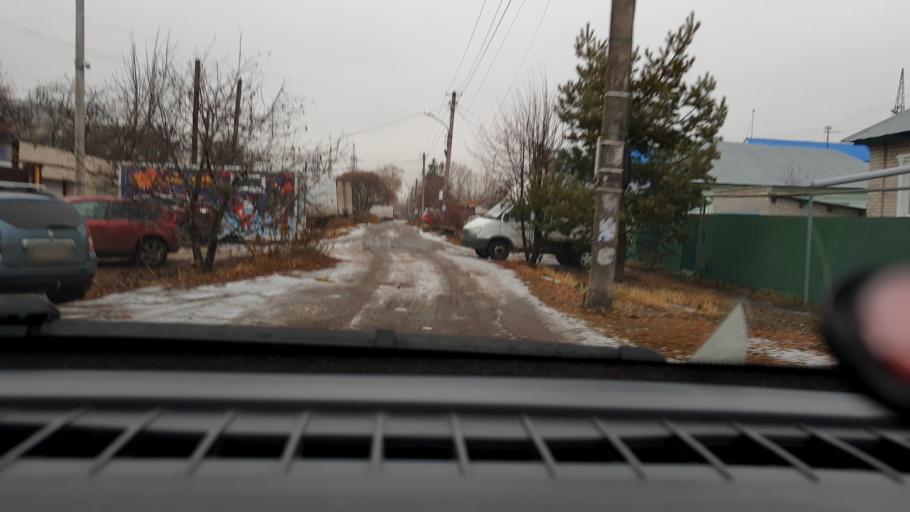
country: RU
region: Nizjnij Novgorod
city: Nizhniy Novgorod
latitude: 56.2924
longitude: 43.8949
